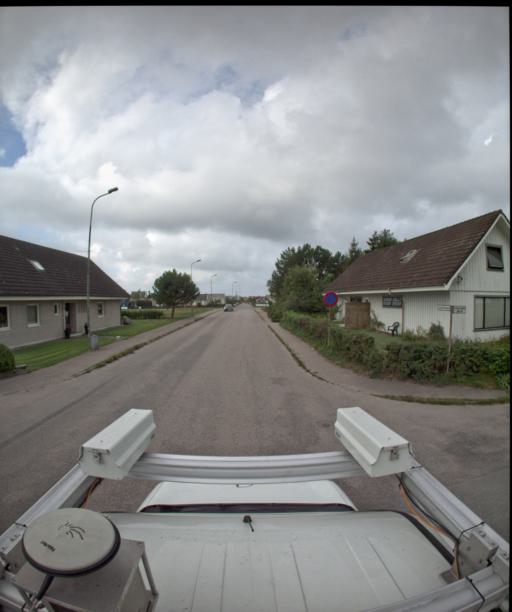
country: SE
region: Halland
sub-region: Falkenbergs Kommun
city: Falkenberg
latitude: 56.8856
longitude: 12.5086
